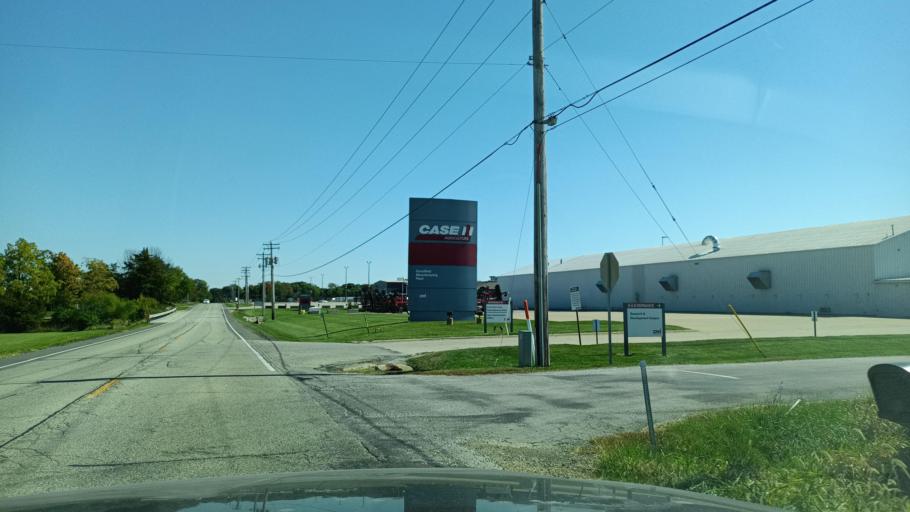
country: US
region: Illinois
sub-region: Woodford County
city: Eureka
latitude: 40.6273
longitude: -89.2657
